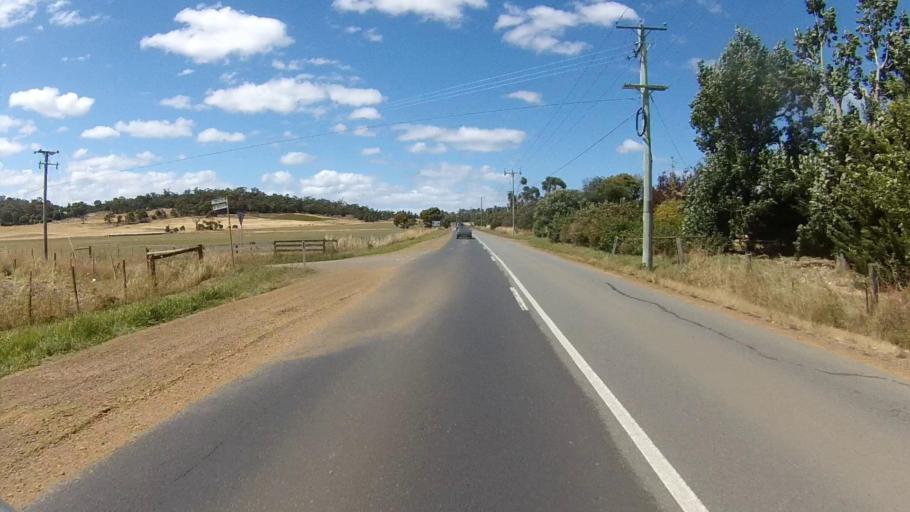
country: AU
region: Tasmania
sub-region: Clarence
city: Cambridge
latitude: -42.8157
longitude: 147.4350
